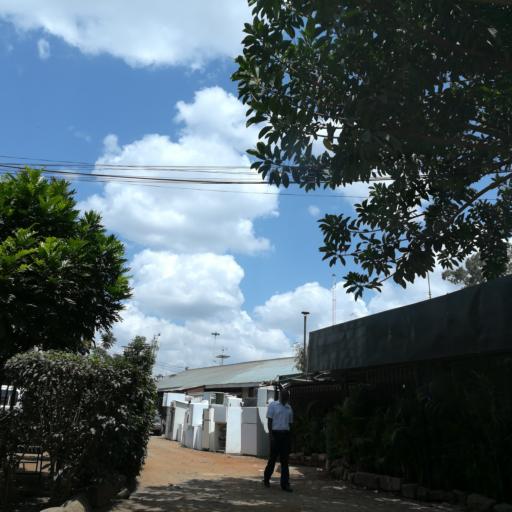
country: KE
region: Nairobi Area
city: Nairobi
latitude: -1.3167
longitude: 36.8150
